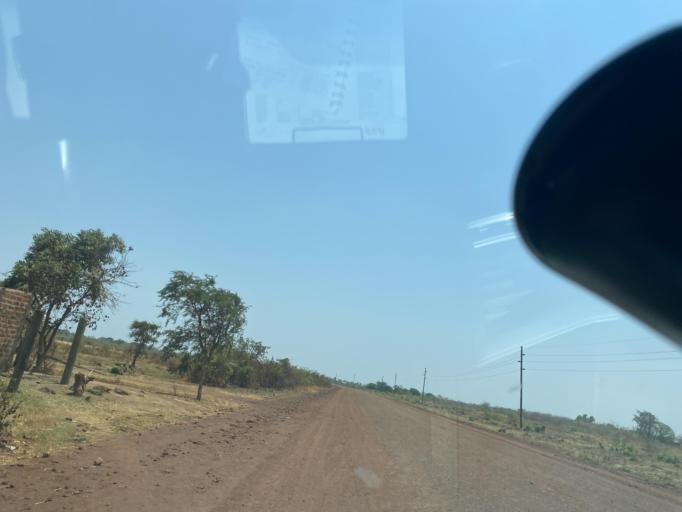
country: ZM
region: Southern
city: Nakambala
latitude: -15.4860
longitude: 27.9004
